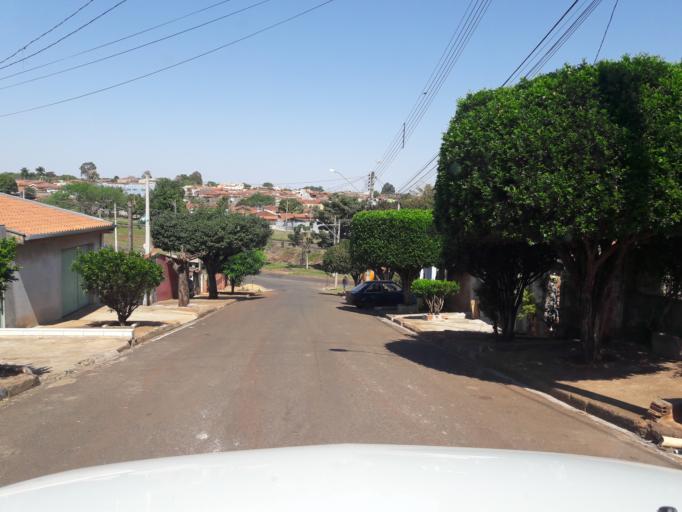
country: BR
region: Sao Paulo
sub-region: Moji-Guacu
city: Mogi-Gaucu
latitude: -22.3405
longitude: -46.9346
